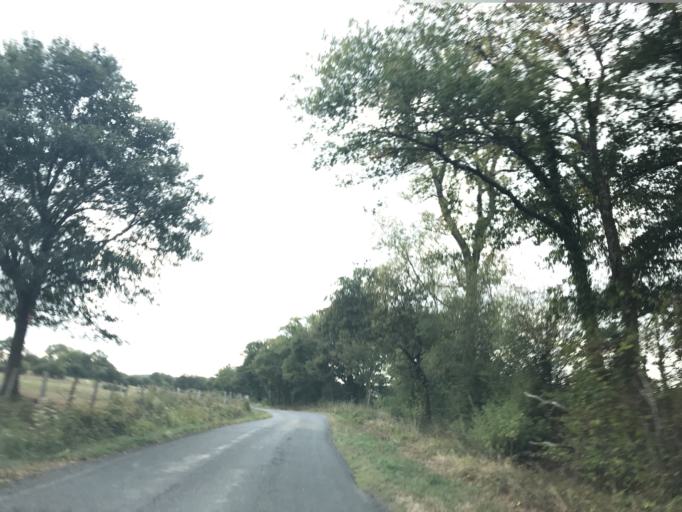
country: FR
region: Auvergne
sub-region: Departement du Puy-de-Dome
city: Courpiere
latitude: 45.7824
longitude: 3.5577
